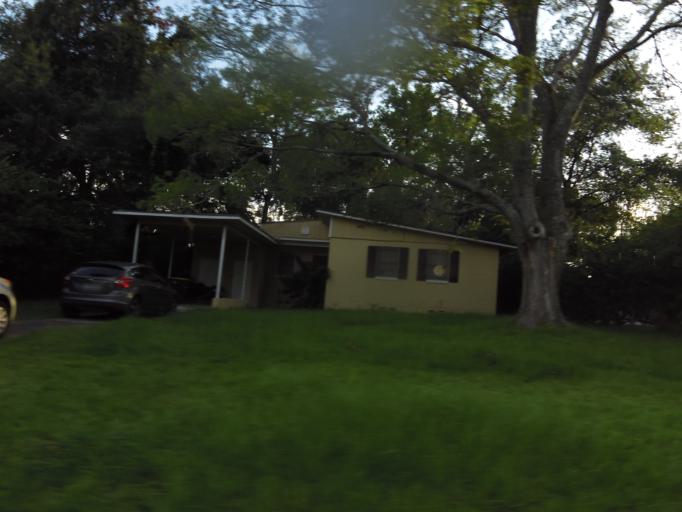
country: US
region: Florida
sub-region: Clay County
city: Orange Park
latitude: 30.2157
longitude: -81.7091
